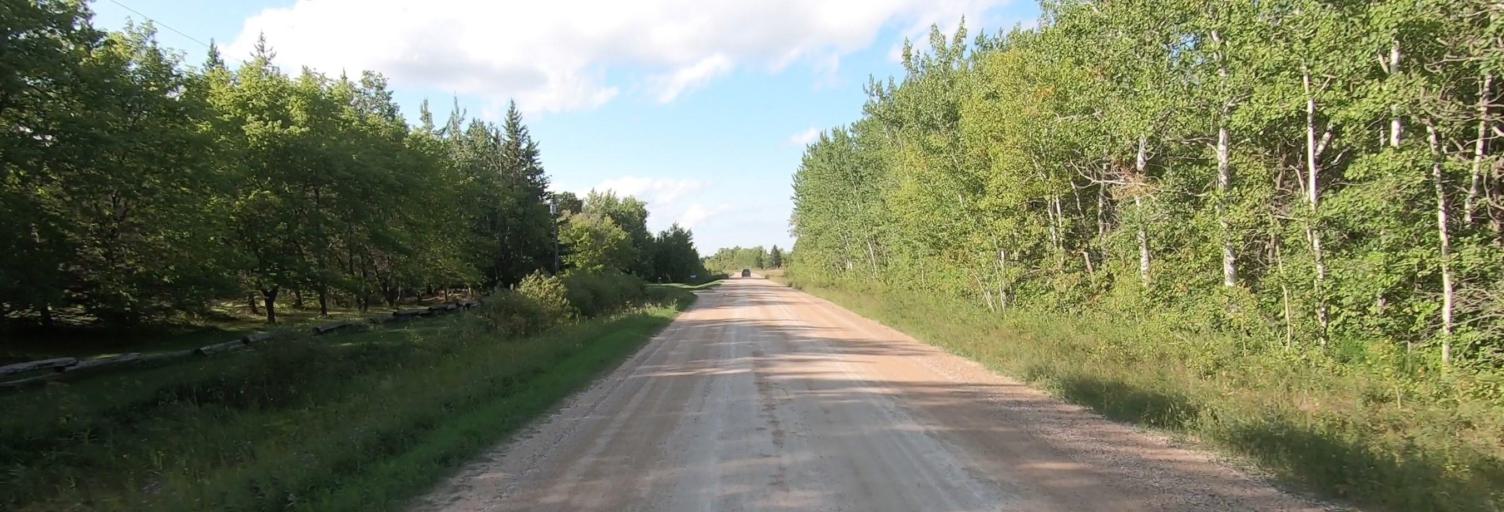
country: CA
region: Manitoba
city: Selkirk
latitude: 50.2406
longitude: -96.8440
